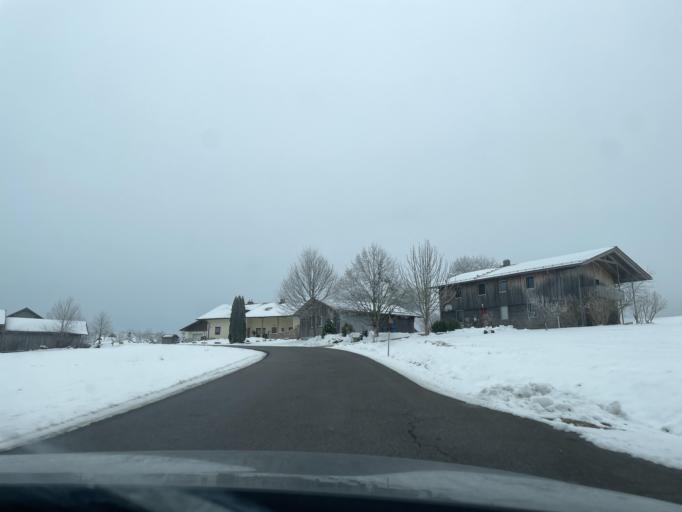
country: DE
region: Bavaria
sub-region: Lower Bavaria
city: Kollnburg
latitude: 49.0131
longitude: 12.9022
